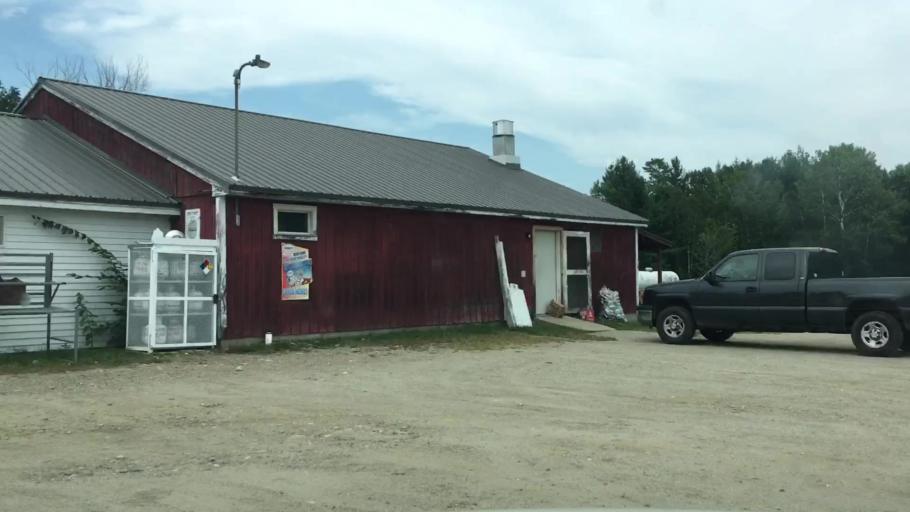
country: US
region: Maine
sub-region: Oxford County
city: Rumford
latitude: 44.6346
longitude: -70.7502
